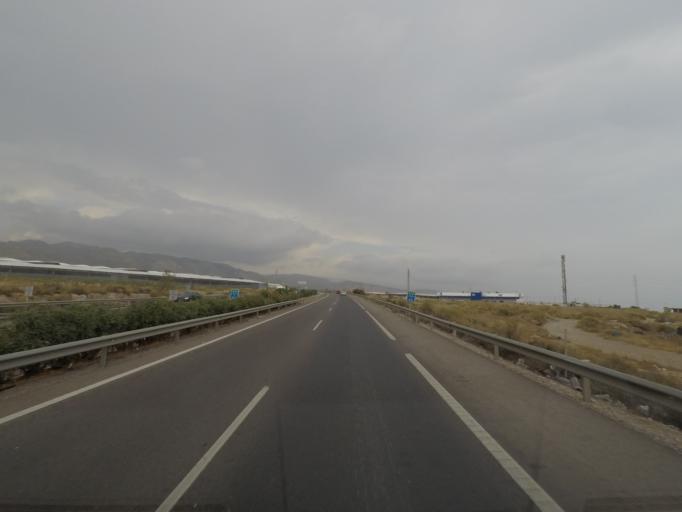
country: ES
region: Andalusia
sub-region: Provincia de Almeria
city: Vicar
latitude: 36.7991
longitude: -2.6806
